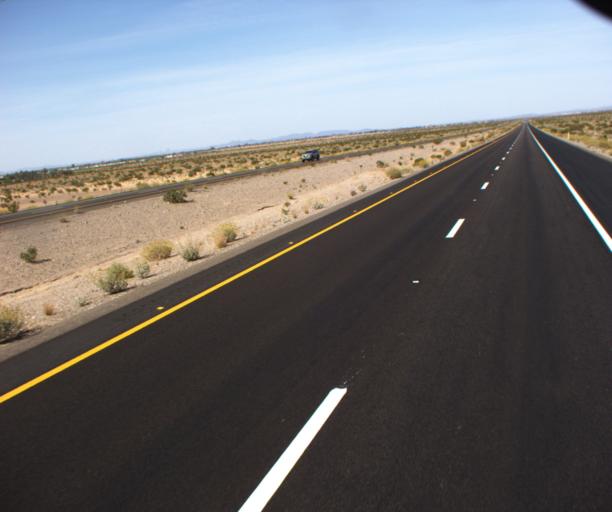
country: US
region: Arizona
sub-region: Yuma County
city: Somerton
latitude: 32.5651
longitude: -114.5591
